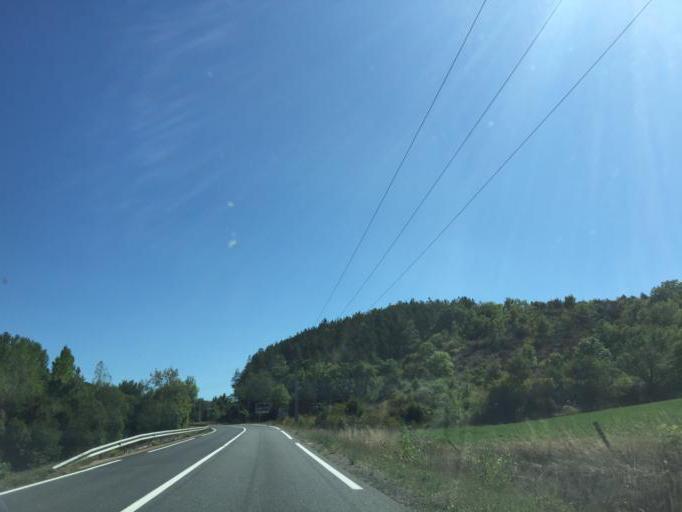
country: FR
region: Midi-Pyrenees
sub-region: Departement de l'Aveyron
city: Saint-Georges-de-Luzencon
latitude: 43.9874
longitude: 2.9668
